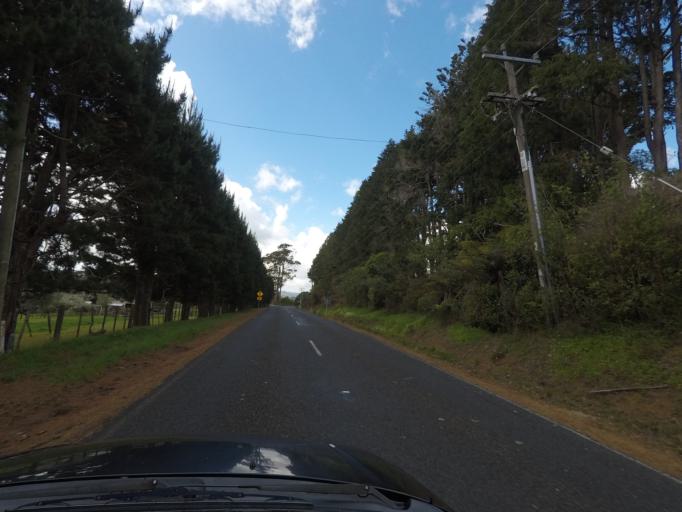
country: NZ
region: Auckland
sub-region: Auckland
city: Pukekohe East
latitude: -37.1451
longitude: 175.0202
